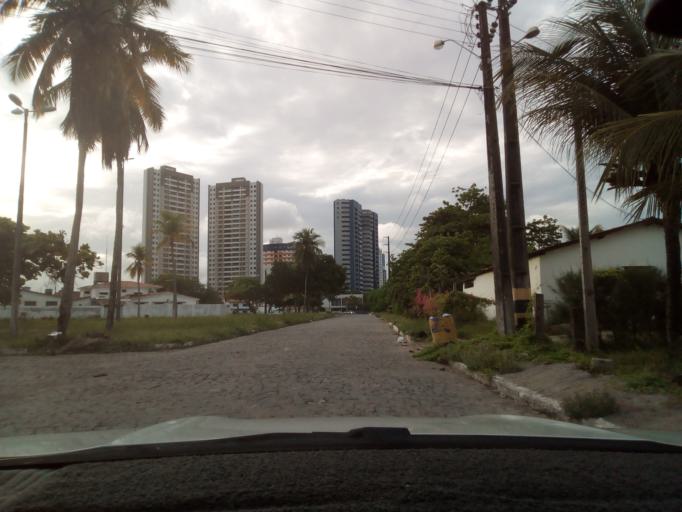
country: BR
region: Paraiba
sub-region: Joao Pessoa
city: Joao Pessoa
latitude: -7.1118
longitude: -34.8378
